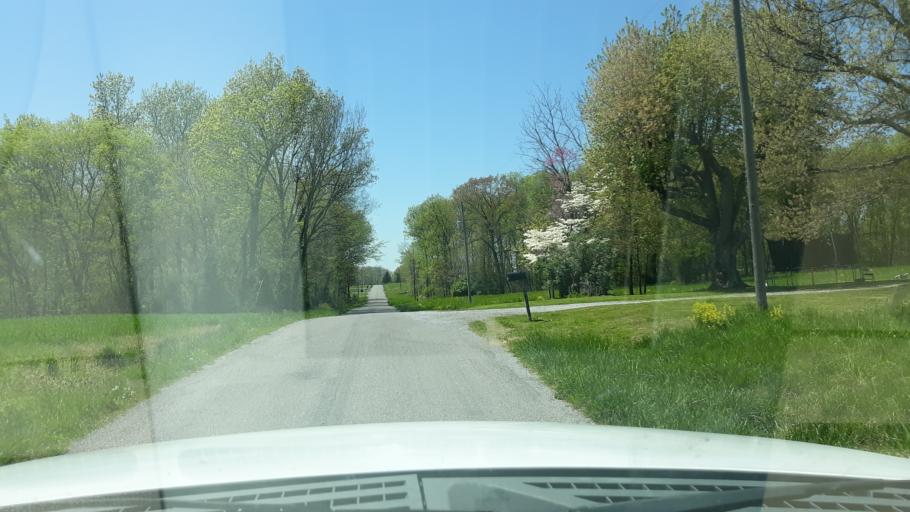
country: US
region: Illinois
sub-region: Saline County
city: Harrisburg
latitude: 37.8849
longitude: -88.6535
